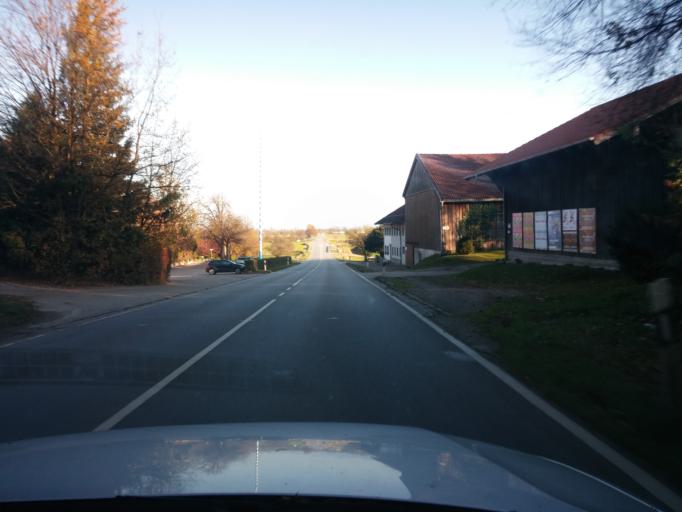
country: DE
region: Bavaria
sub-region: Upper Bavaria
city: Bruckmuhl
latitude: 47.8914
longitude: 11.9103
